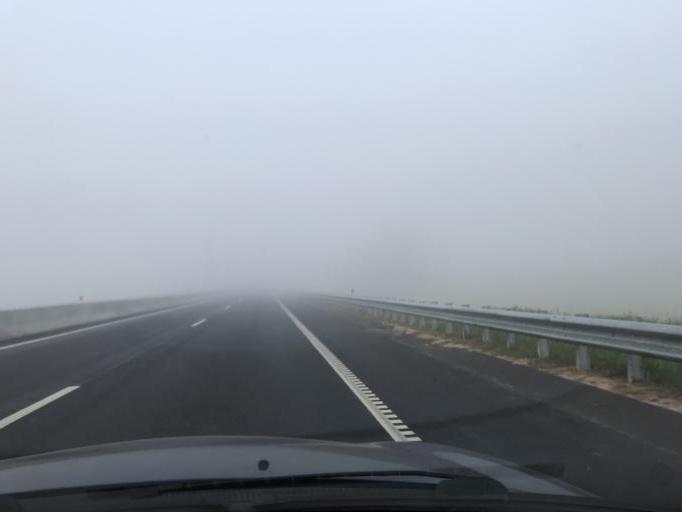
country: BY
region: Minsk
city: Valozhyn
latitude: 54.0411
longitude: 26.6837
